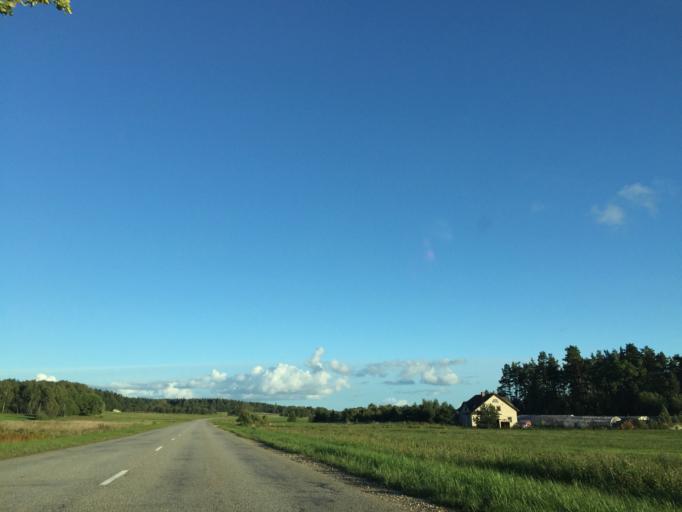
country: LV
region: Kuldigas Rajons
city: Kuldiga
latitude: 56.9311
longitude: 22.0412
